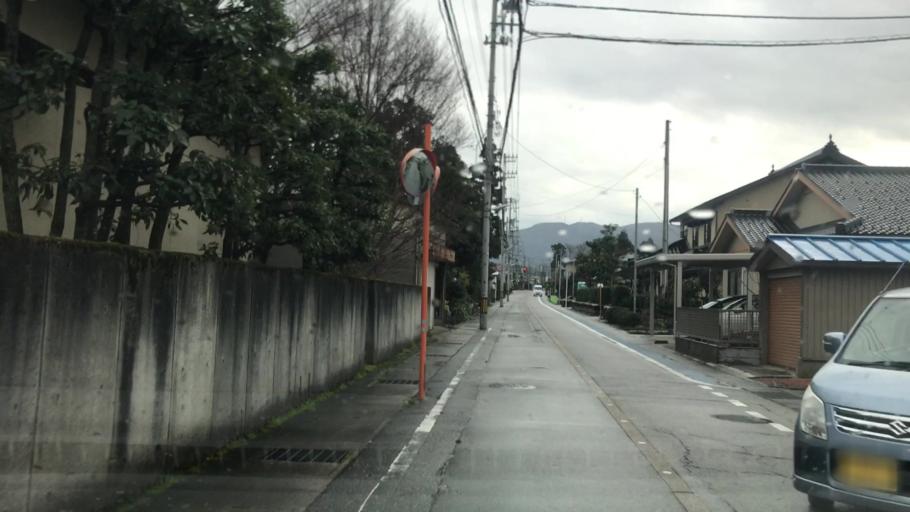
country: JP
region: Toyama
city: Yatsuomachi-higashikumisaka
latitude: 36.5943
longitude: 137.2065
